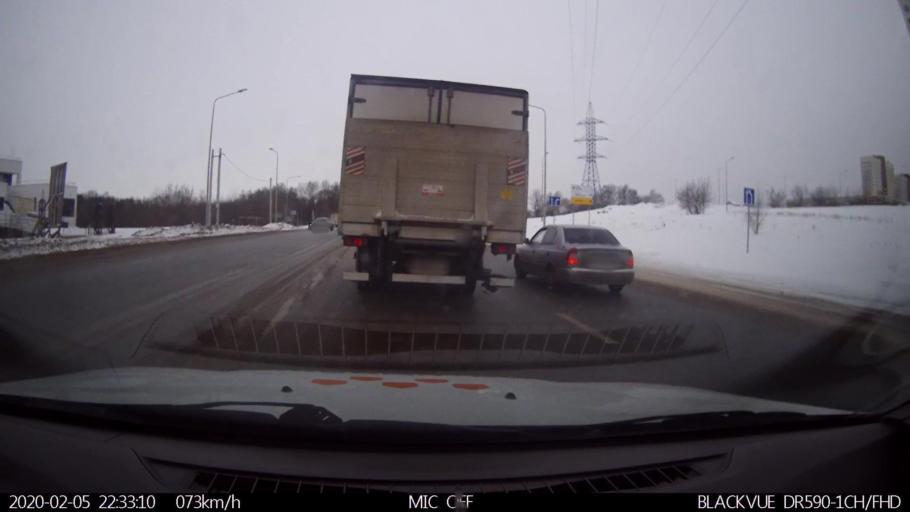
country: RU
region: Nizjnij Novgorod
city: Imeni Stepana Razina
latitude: 54.7365
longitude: 44.2058
